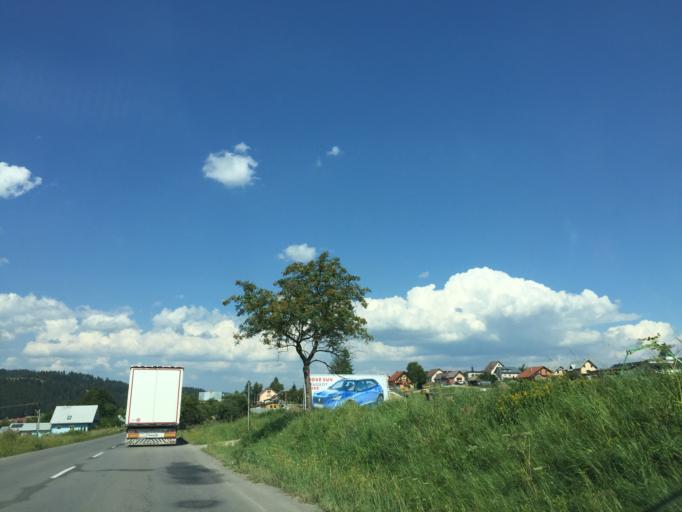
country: SK
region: Zilinsky
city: Namestovo
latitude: 49.3605
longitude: 19.4053
